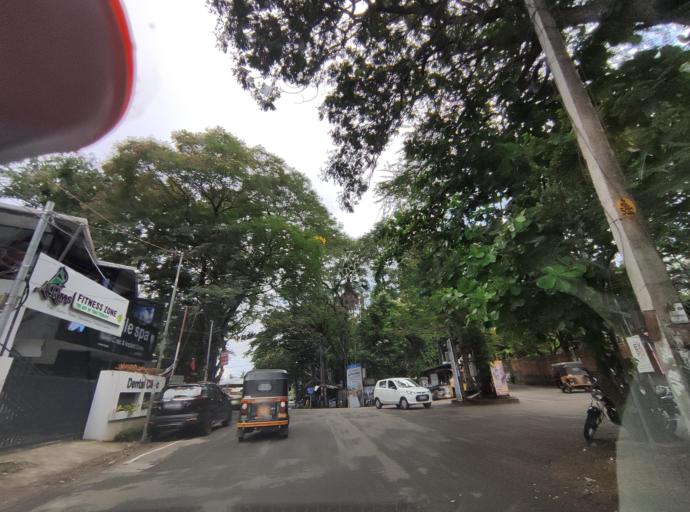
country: IN
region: Kerala
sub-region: Thiruvananthapuram
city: Thiruvananthapuram
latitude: 8.4958
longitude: 76.9624
